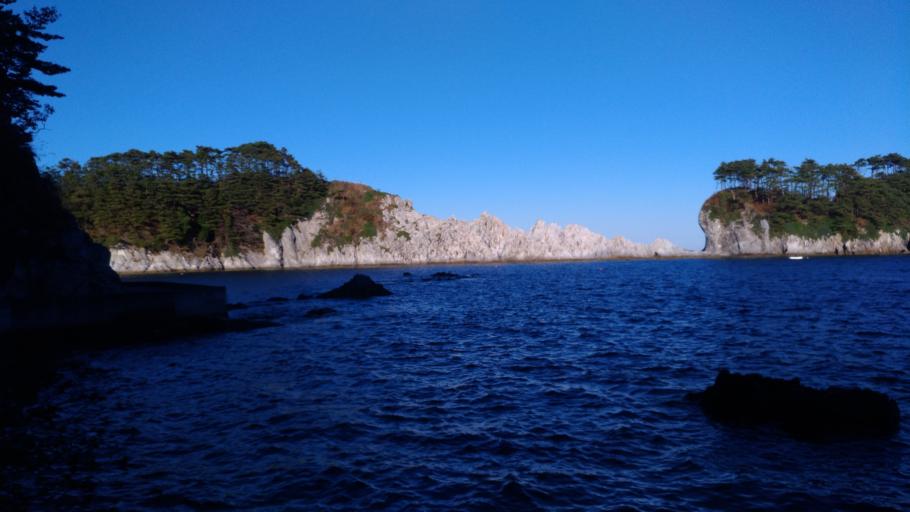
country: JP
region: Iwate
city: Miyako
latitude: 39.6499
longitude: 141.9799
